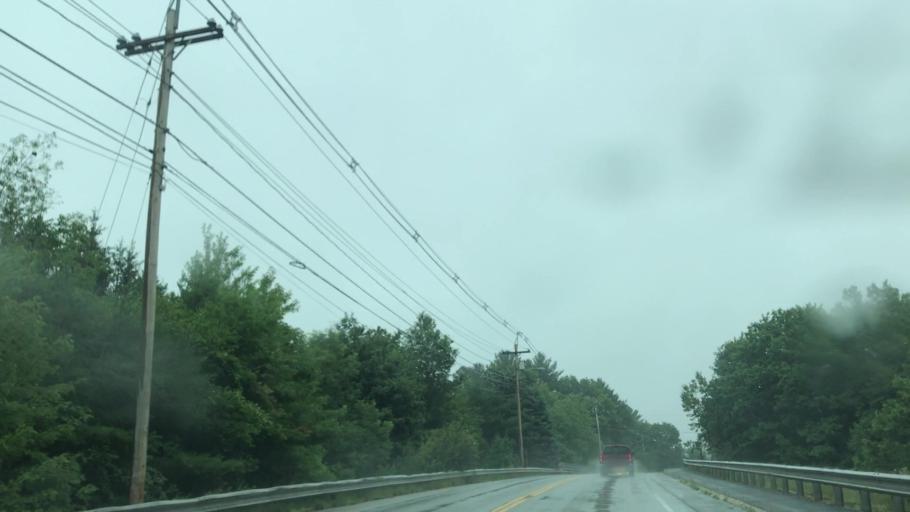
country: US
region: Maine
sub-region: York County
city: North Berwick
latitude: 43.3079
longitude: -70.7237
